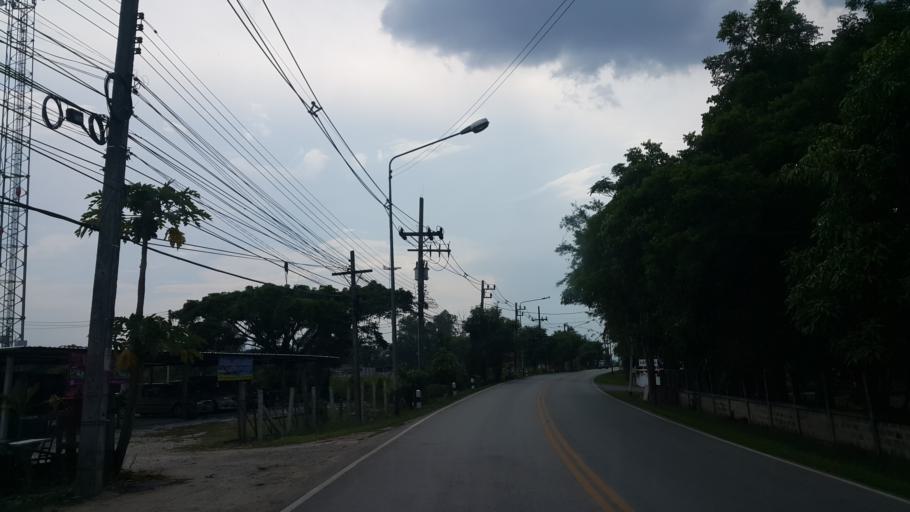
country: TH
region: Chiang Rai
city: Chiang Rai
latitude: 19.9123
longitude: 99.8730
